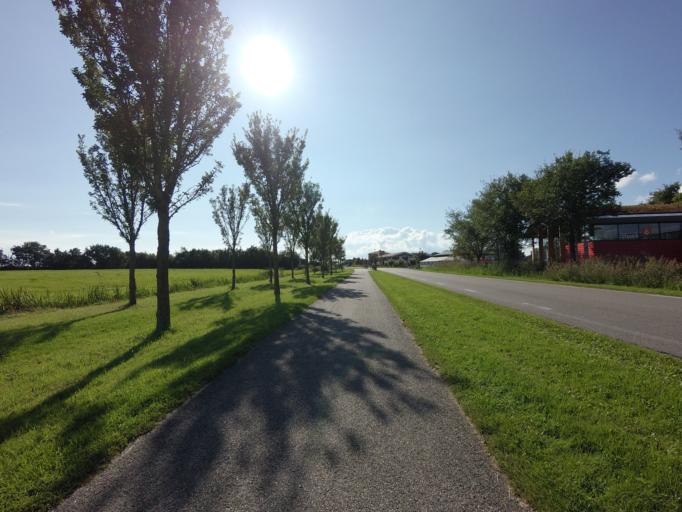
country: NL
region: Friesland
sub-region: Gemeente Terschelling
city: West-Terschelling
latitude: 53.3807
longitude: 5.2870
